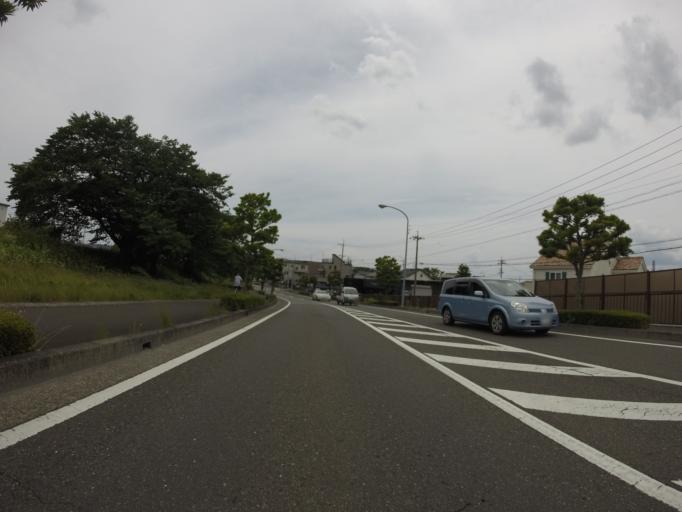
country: JP
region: Shizuoka
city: Shizuoka-shi
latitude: 35.0016
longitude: 138.4212
